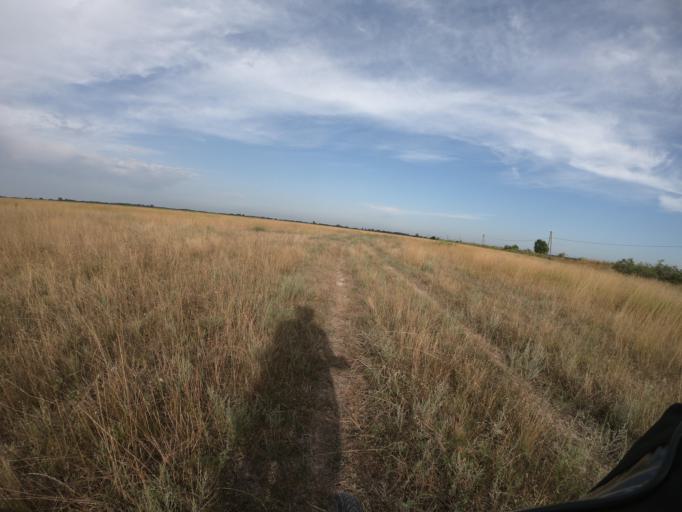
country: HU
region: Hajdu-Bihar
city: Tiszacsege
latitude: 47.6100
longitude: 21.0421
